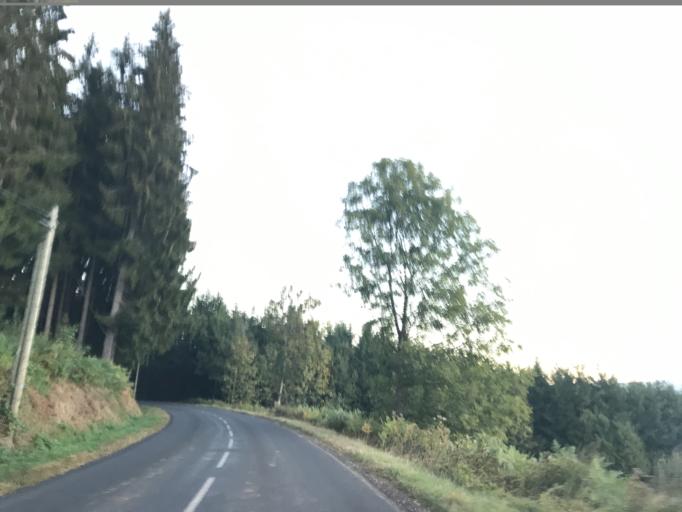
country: FR
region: Auvergne
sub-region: Departement du Puy-de-Dome
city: Celles-sur-Durolle
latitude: 45.8470
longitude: 3.6368
